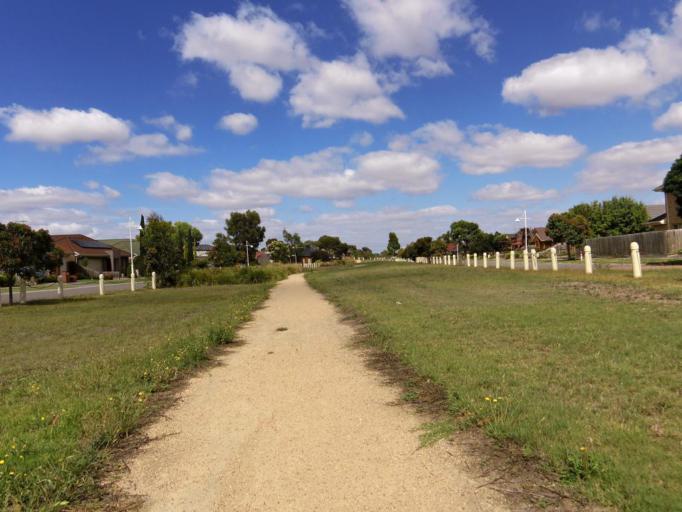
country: AU
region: Victoria
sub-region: Whittlesea
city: Mill Park
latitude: -37.6379
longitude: 145.0753
